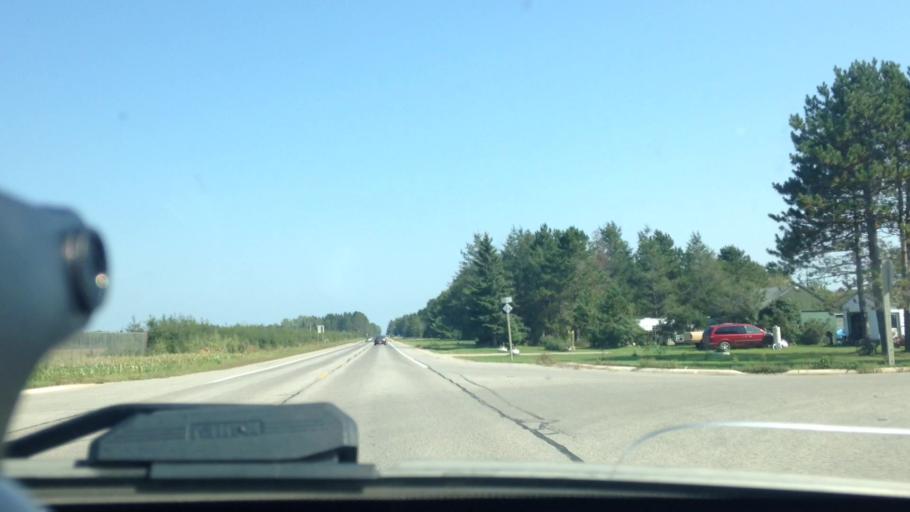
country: US
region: Michigan
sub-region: Luce County
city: Newberry
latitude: 46.3035
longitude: -85.4577
